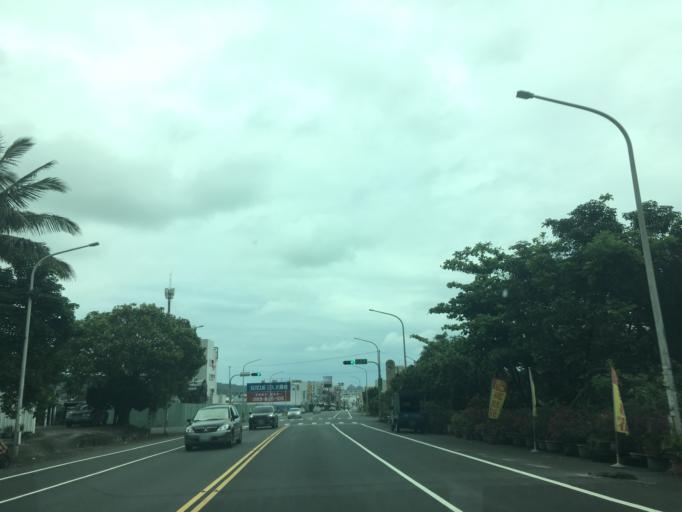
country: TW
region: Taiwan
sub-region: Taitung
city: Taitung
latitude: 23.1015
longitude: 121.3730
